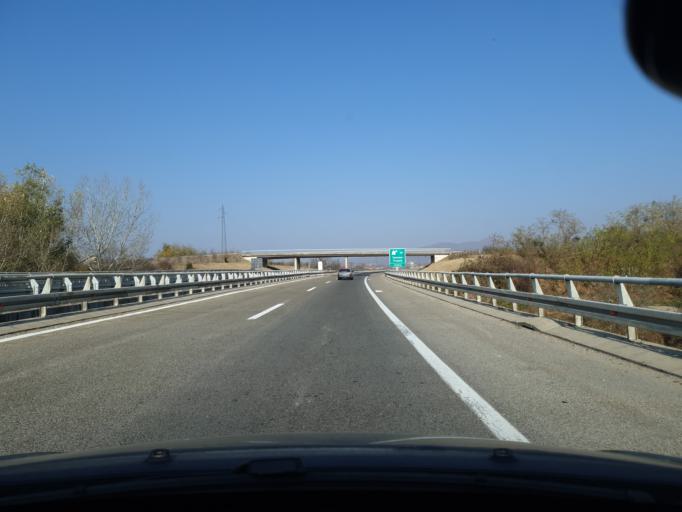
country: RS
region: Central Serbia
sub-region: Nisavski Okrug
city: Nis
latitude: 43.3389
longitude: 21.8157
